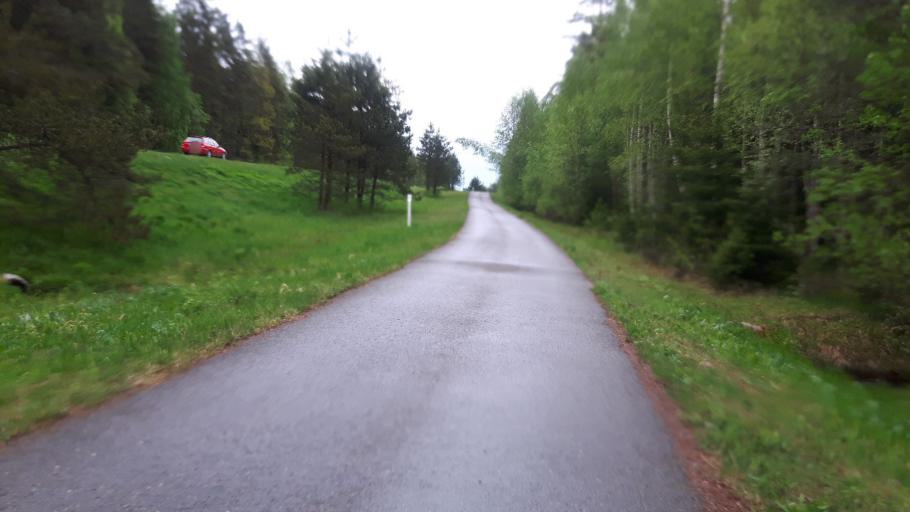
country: FI
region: Kymenlaakso
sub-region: Kotka-Hamina
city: Hamina
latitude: 60.5644
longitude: 27.0815
